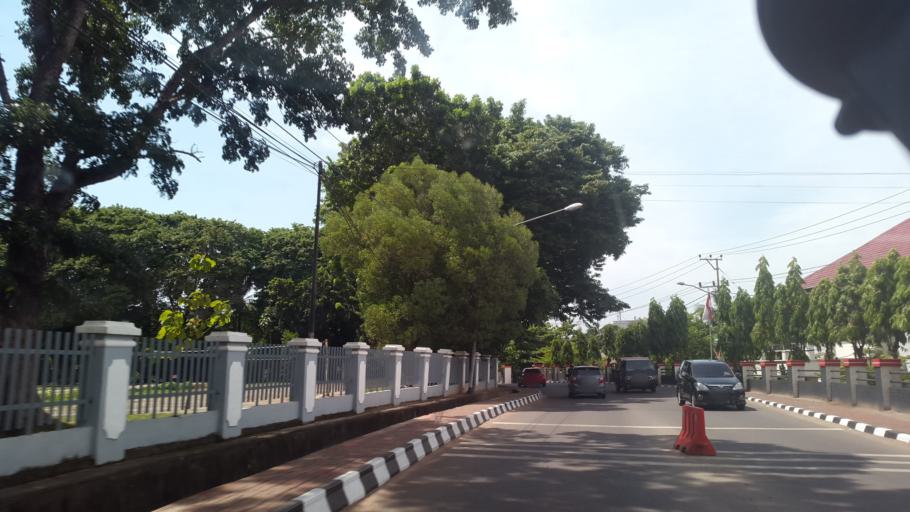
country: ID
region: South Sumatra
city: Plaju
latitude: -2.9890
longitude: 104.7295
